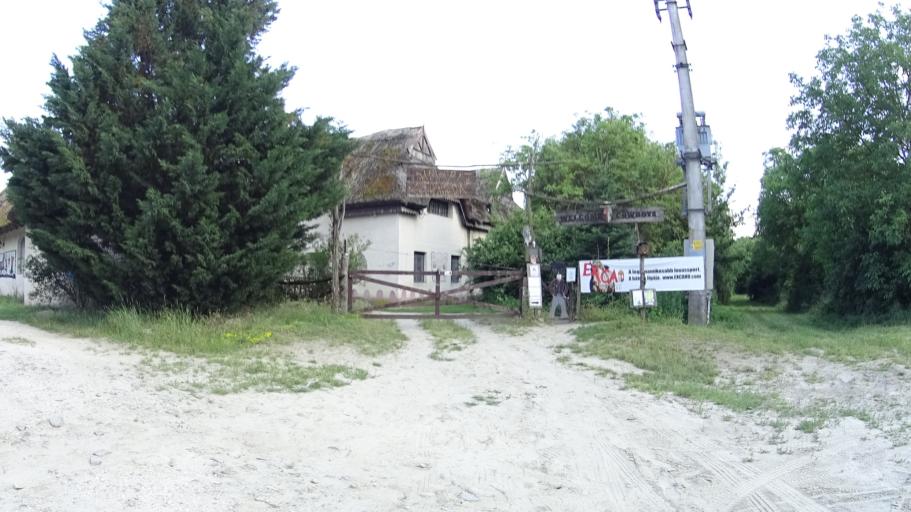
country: HU
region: Pest
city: Dunabogdany
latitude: 47.7996
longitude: 19.0454
